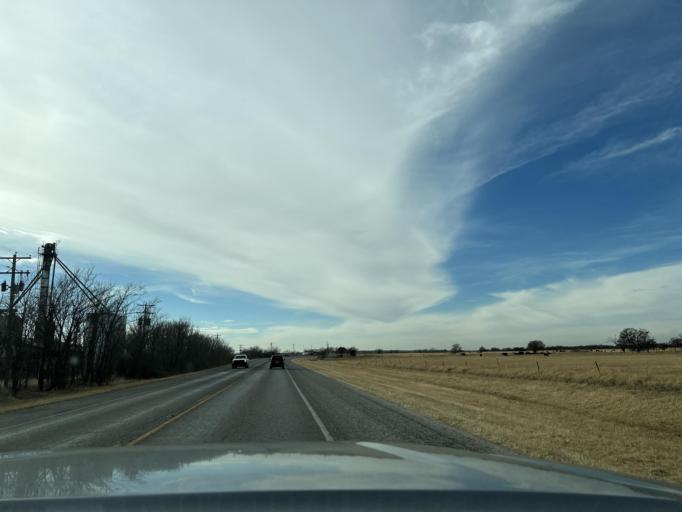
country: US
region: Texas
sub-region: Fisher County
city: Roby
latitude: 32.7542
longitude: -100.2594
